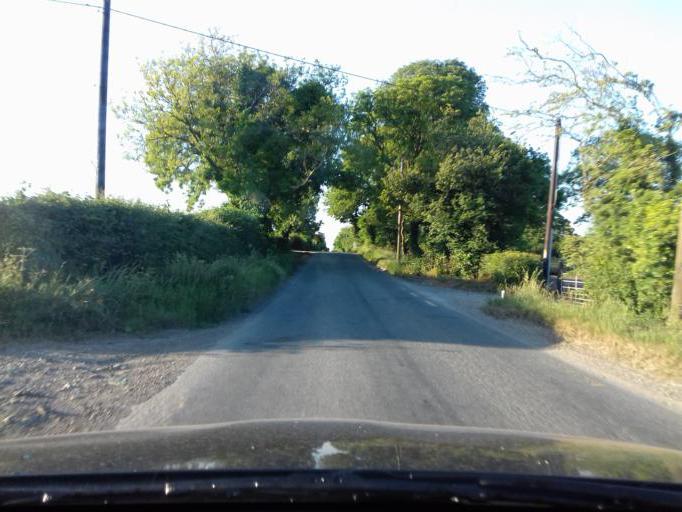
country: IE
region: Leinster
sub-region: An Mhi
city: Ashbourne
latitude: 53.5709
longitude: -6.3812
